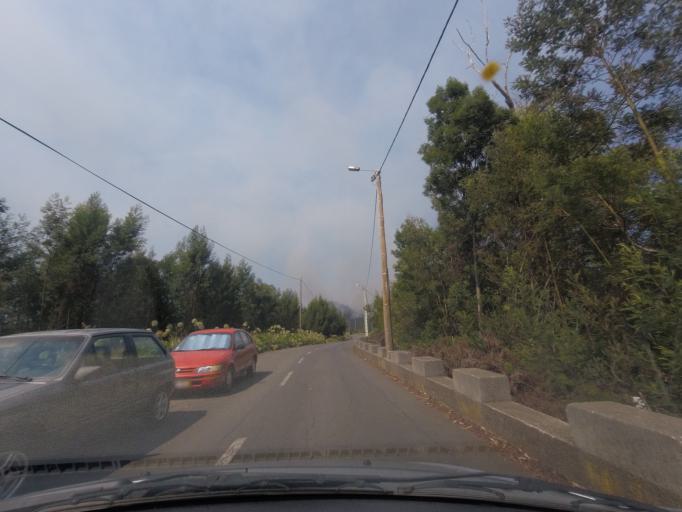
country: PT
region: Madeira
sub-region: Ribeira Brava
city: Campanario
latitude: 32.6897
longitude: -17.0572
